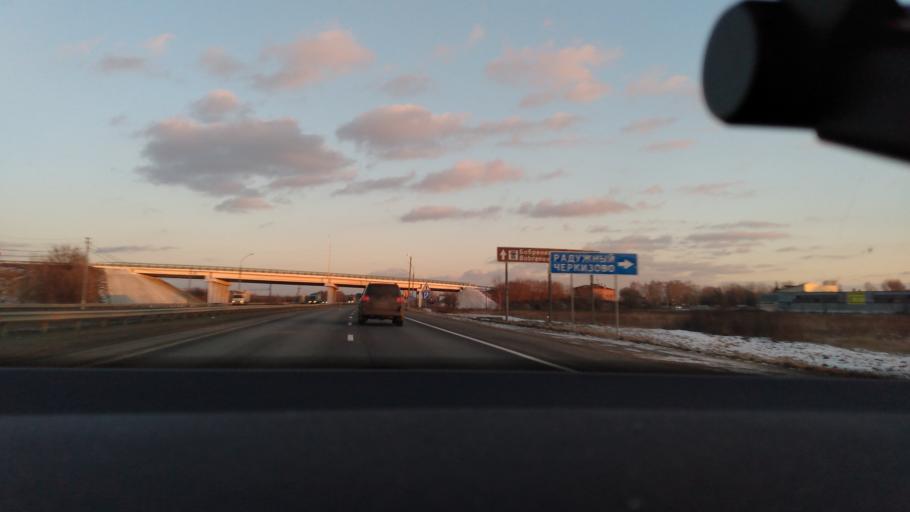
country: RU
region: Moskovskaya
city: Raduzhnyy
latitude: 55.1464
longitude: 38.7269
